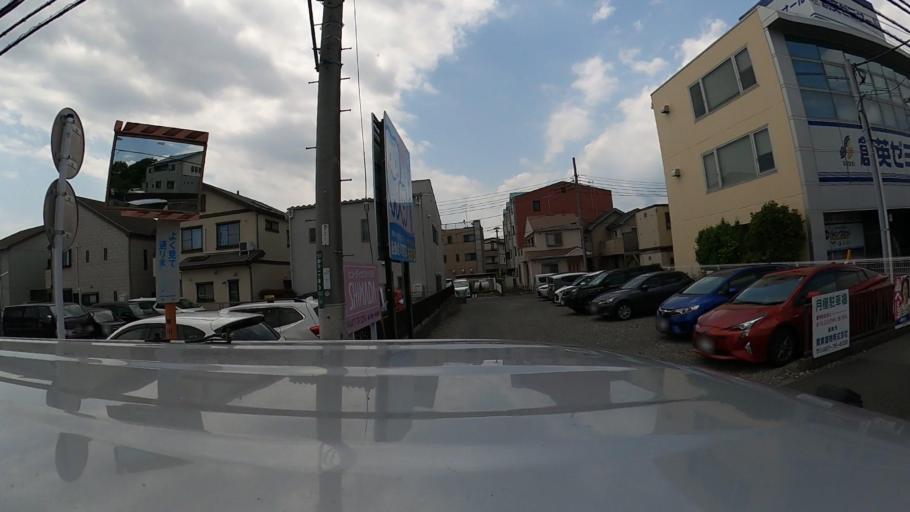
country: JP
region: Kanagawa
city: Chigasaki
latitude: 35.3689
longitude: 139.3895
